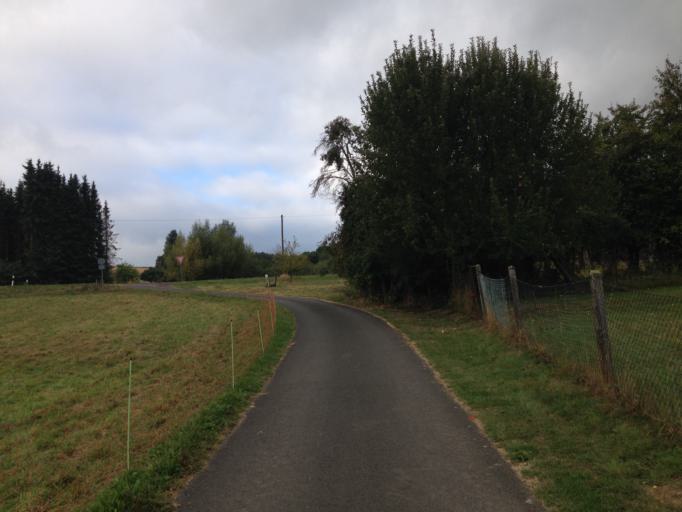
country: DE
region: Hesse
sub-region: Regierungsbezirk Giessen
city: Lohra
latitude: 50.6742
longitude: 8.5679
